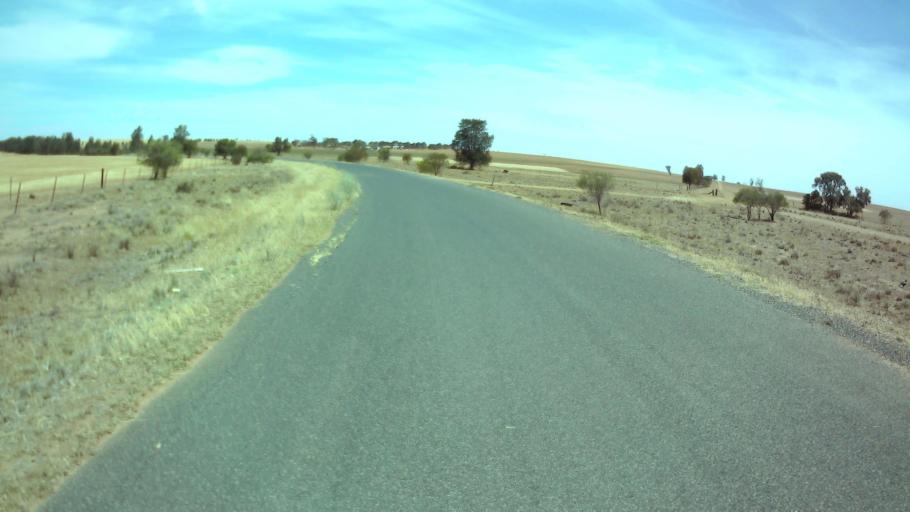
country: AU
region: New South Wales
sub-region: Weddin
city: Grenfell
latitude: -33.8885
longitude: 147.7416
